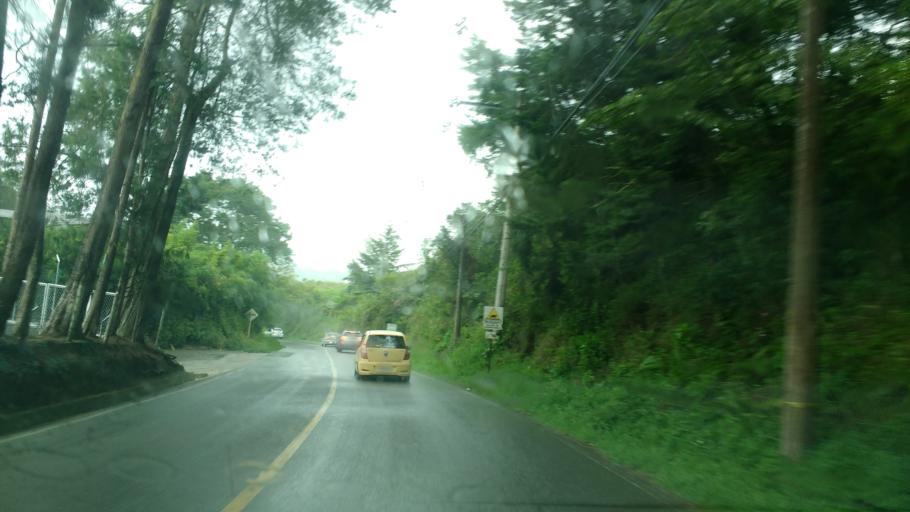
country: CO
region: Antioquia
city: Marinilla
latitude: 6.1730
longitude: -75.3224
